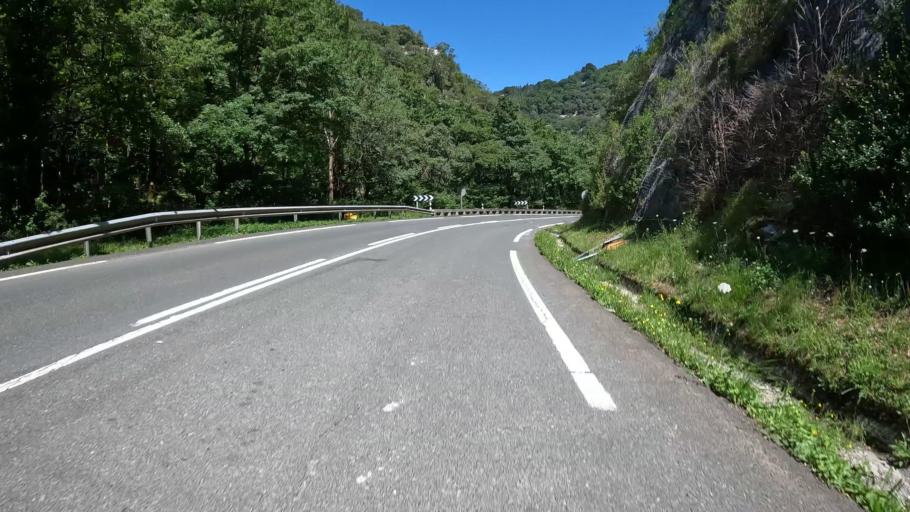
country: ES
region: Basque Country
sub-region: Provincia de Guipuzcoa
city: Oreja
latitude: 43.0773
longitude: -2.0173
